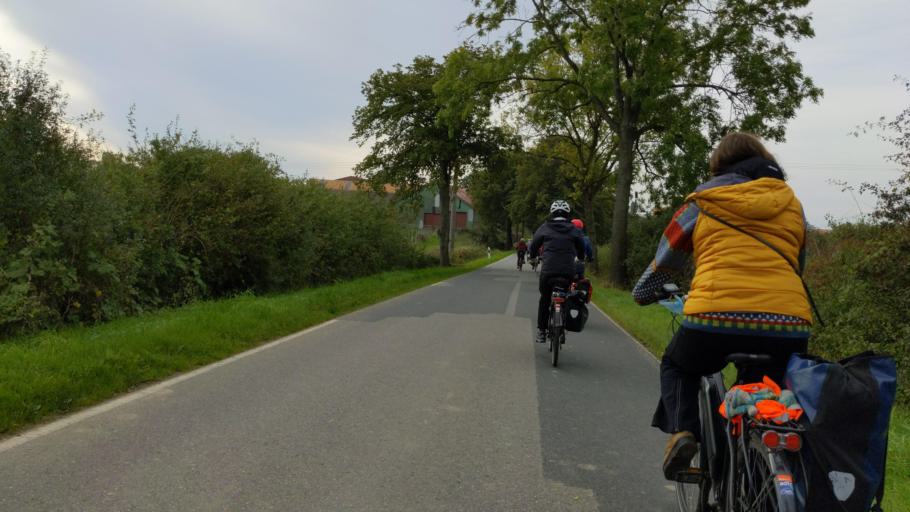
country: DE
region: Schleswig-Holstein
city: Rehhorst
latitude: 53.8787
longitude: 10.4728
